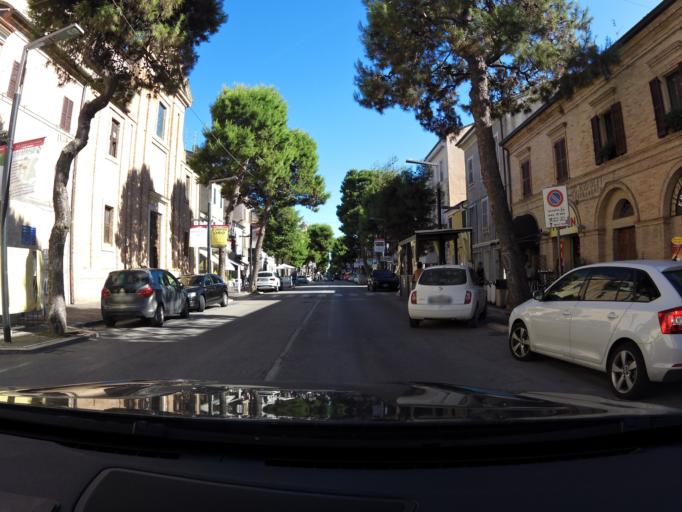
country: IT
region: The Marches
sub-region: Provincia di Macerata
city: Porto Recanati
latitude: 43.4346
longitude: 13.6628
